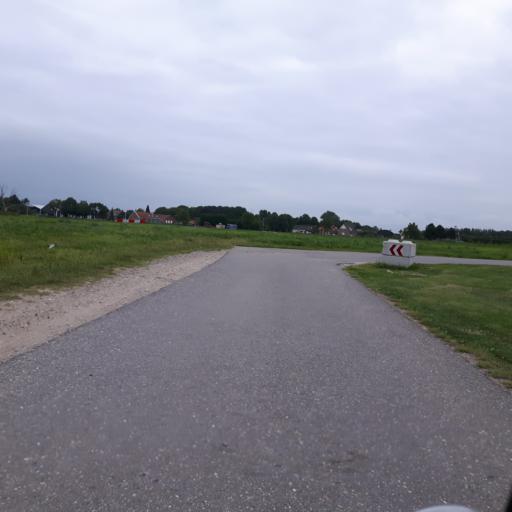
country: NL
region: Zeeland
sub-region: Gemeente Goes
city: Goes
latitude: 51.4855
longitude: 3.8977
